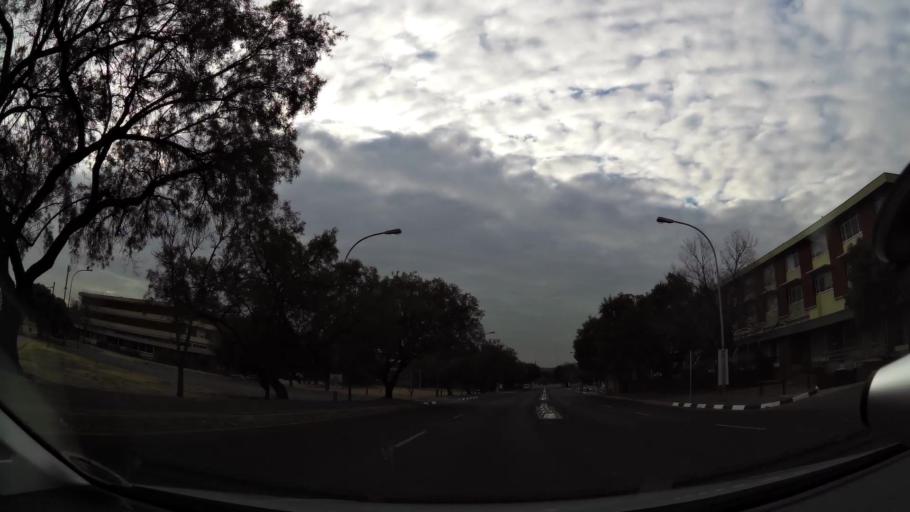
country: ZA
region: Orange Free State
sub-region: Mangaung Metropolitan Municipality
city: Bloemfontein
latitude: -29.1082
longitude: 26.1893
